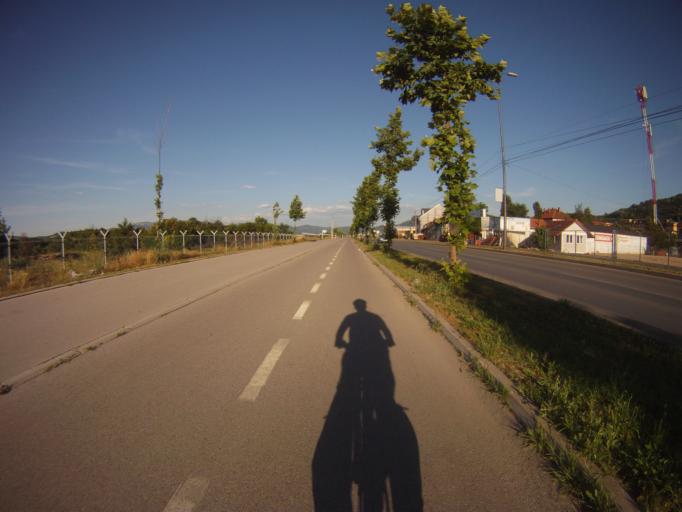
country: RS
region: Central Serbia
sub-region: Nisavski Okrug
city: Nis
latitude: 43.3093
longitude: 21.9423
